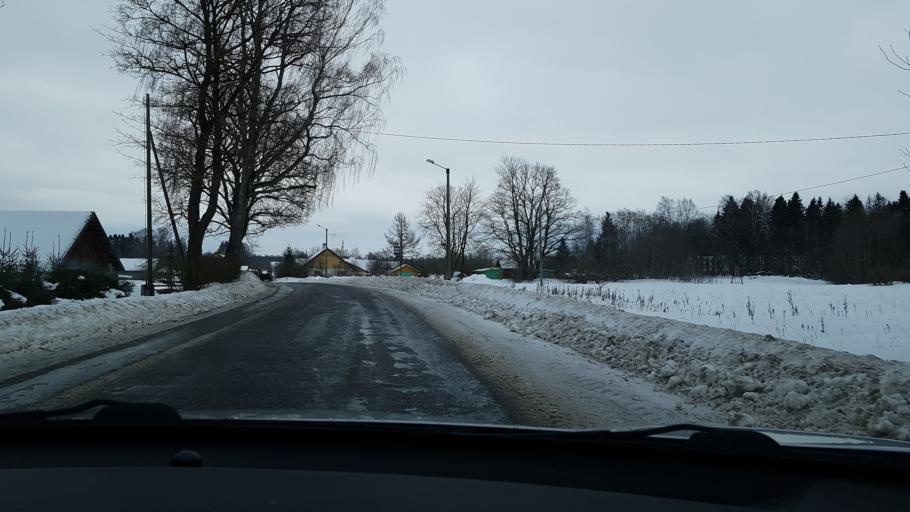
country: EE
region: Jaervamaa
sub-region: Koeru vald
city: Koeru
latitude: 58.9733
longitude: 26.0066
